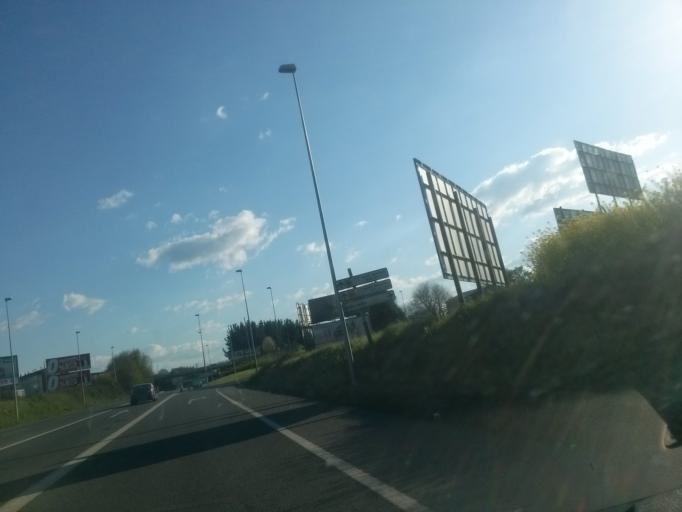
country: ES
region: Galicia
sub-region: Provincia de Lugo
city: Lugo
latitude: 43.0308
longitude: -7.5734
